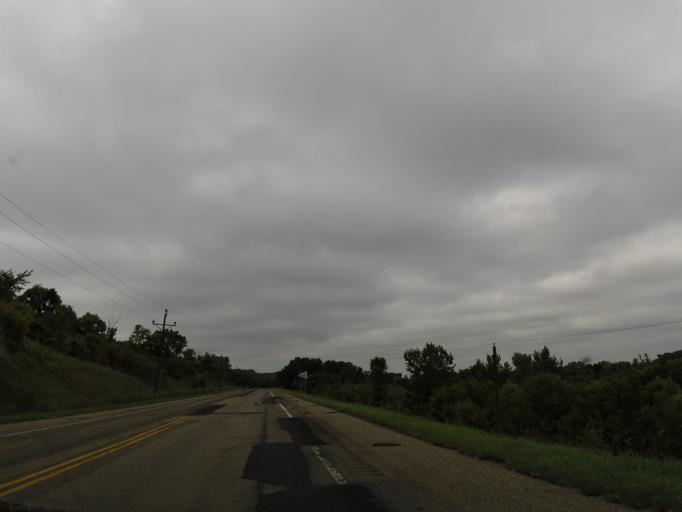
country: US
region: Minnesota
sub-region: Yellow Medicine County
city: Granite Falls
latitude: 44.8342
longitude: -95.6083
